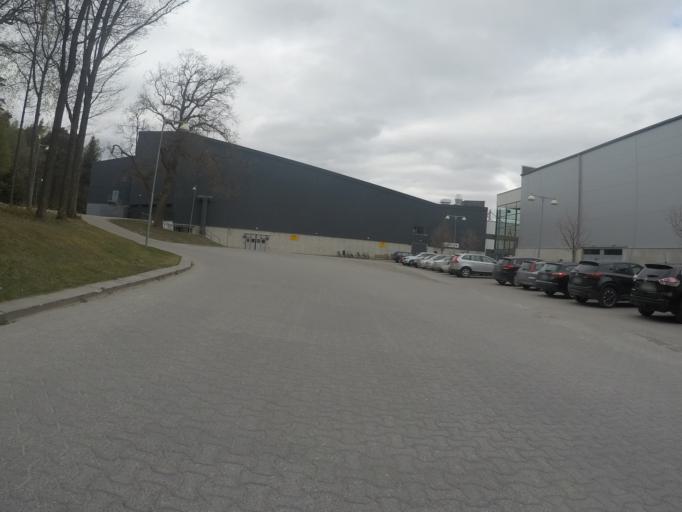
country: SE
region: Vaestmanland
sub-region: Vasteras
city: Vasteras
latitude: 59.6254
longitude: 16.5292
